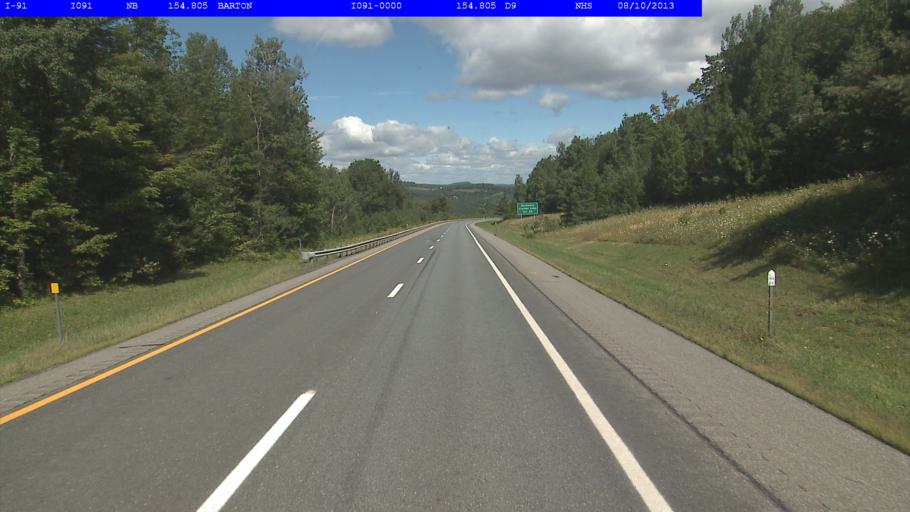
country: US
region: Vermont
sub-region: Orleans County
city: Newport
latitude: 44.7202
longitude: -72.1774
